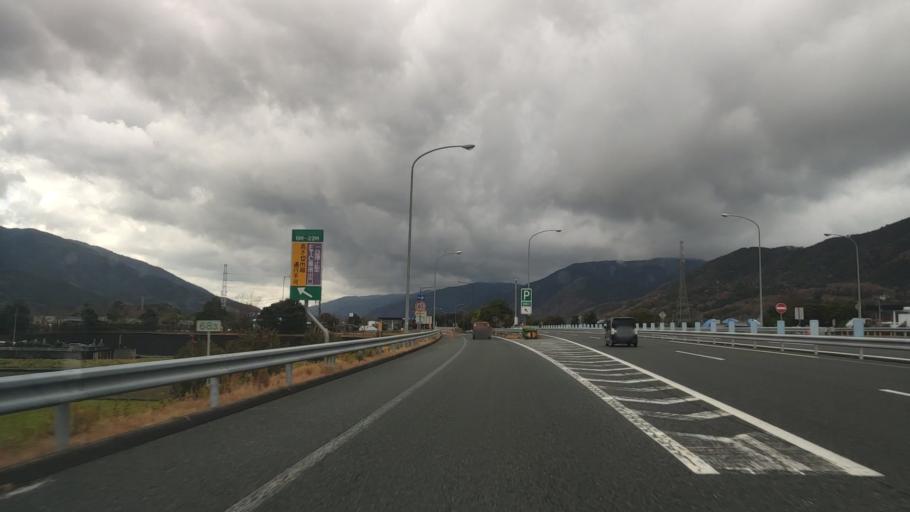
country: JP
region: Tokushima
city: Ikedacho
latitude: 34.0376
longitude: 133.8965
